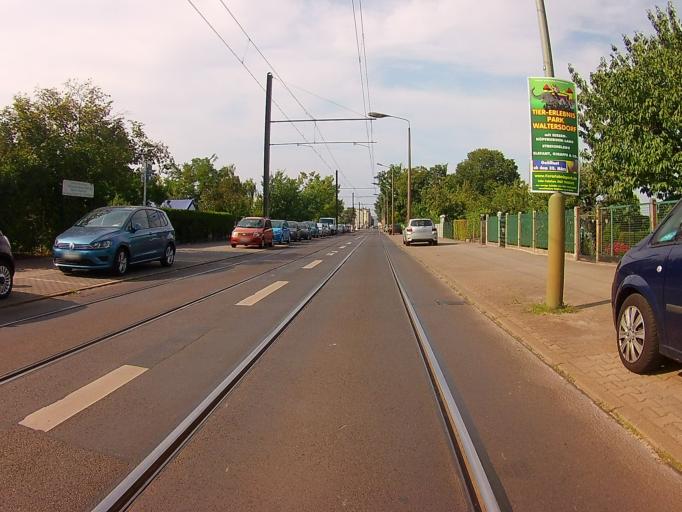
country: DE
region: Berlin
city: Kopenick Bezirk
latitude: 52.4335
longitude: 13.5714
